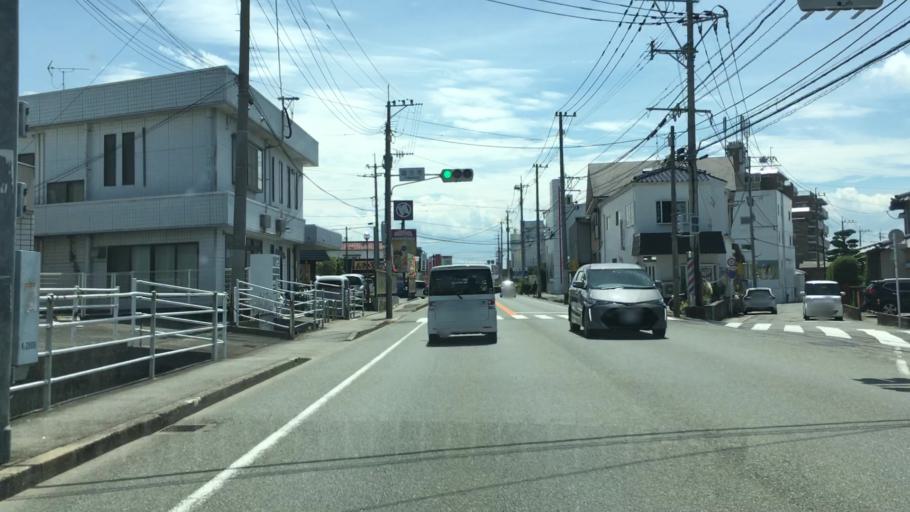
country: JP
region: Fukuoka
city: Dazaifu
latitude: 33.5178
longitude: 130.5024
